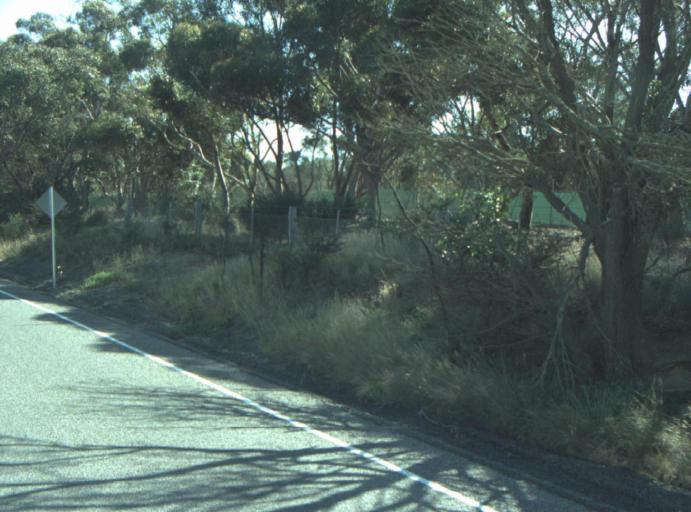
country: AU
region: Victoria
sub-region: Greater Geelong
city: Lara
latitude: -37.9098
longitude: 144.3985
